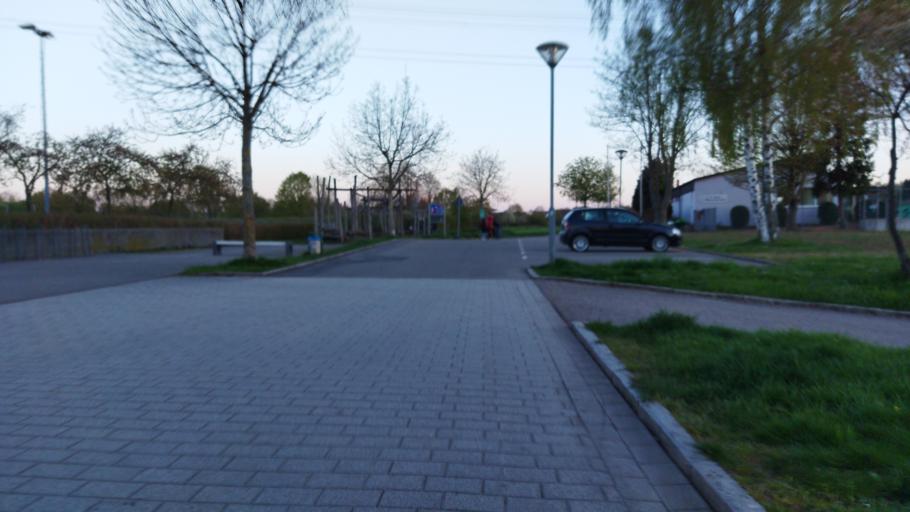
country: DE
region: Baden-Wuerttemberg
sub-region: Regierungsbezirk Stuttgart
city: Untereisesheim
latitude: 49.2048
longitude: 9.2009
